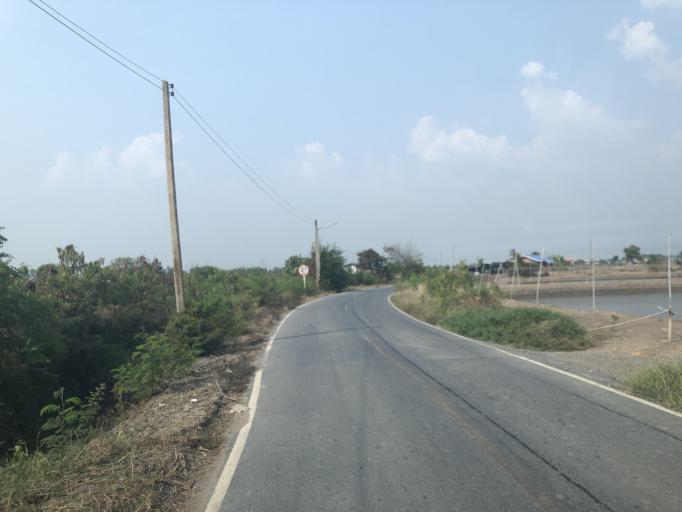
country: TH
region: Chachoengsao
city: Bang Pakong
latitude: 13.5166
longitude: 100.9248
